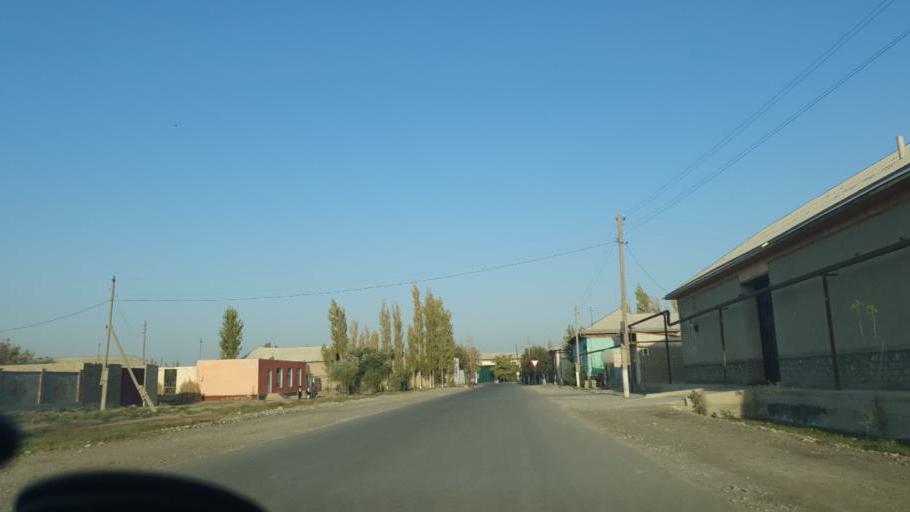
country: UZ
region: Fergana
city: Beshariq
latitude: 40.4676
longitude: 70.5611
